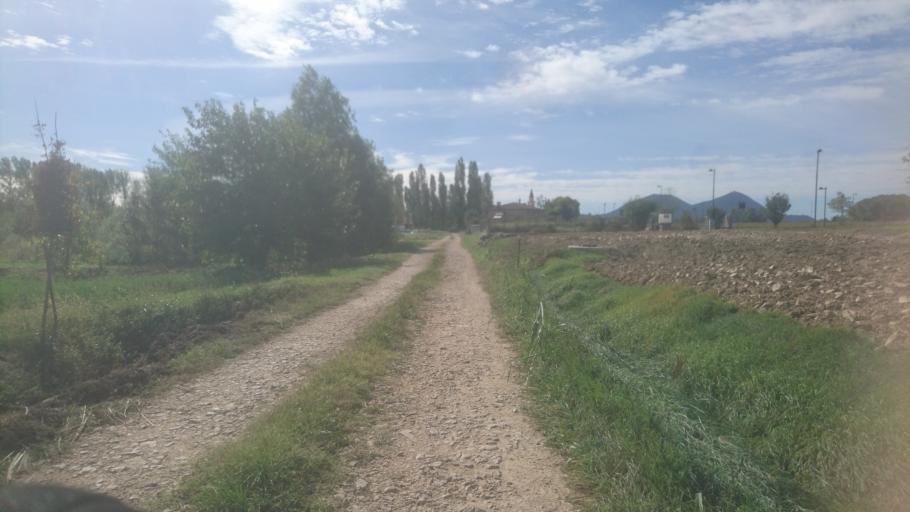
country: IT
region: Veneto
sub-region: Provincia di Padova
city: Veggiano
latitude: 45.4199
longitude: 11.7221
